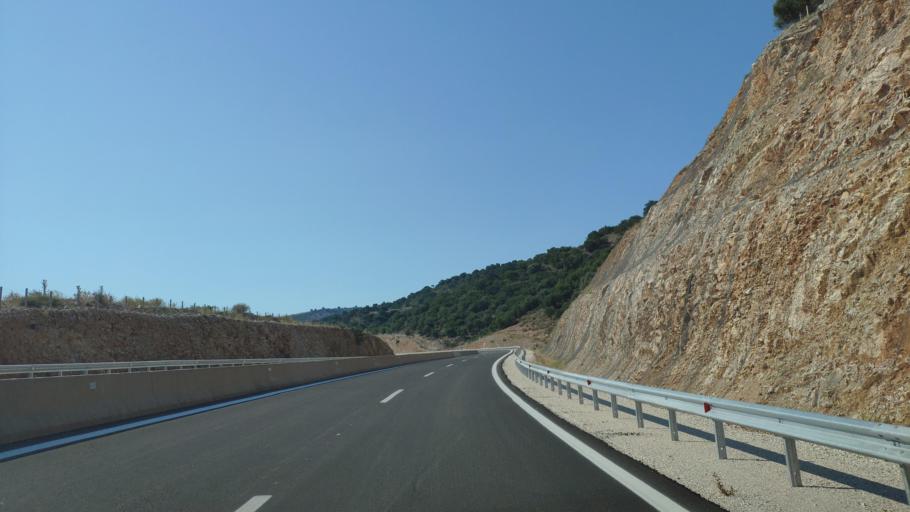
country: GR
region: West Greece
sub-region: Nomos Aitolias kai Akarnanias
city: Katouna
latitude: 38.8336
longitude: 21.1167
